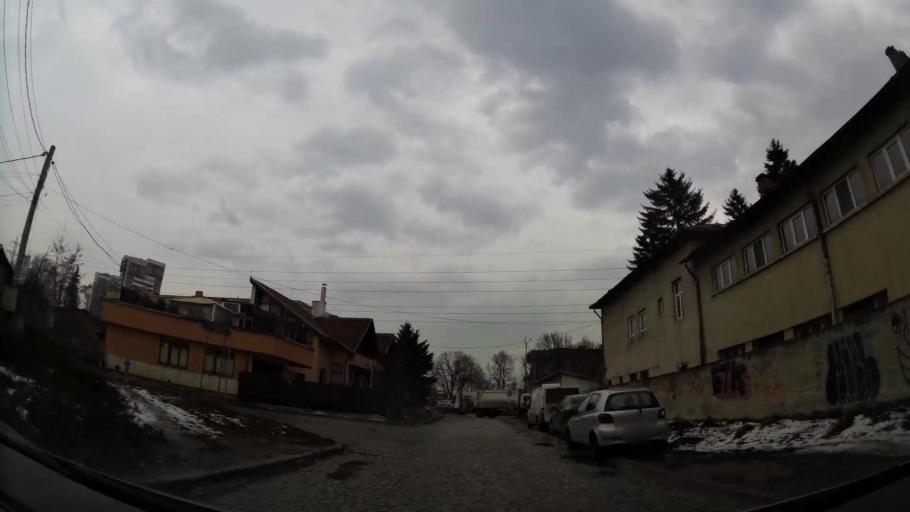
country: BG
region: Sofia-Capital
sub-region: Stolichna Obshtina
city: Sofia
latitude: 42.6699
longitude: 23.2530
